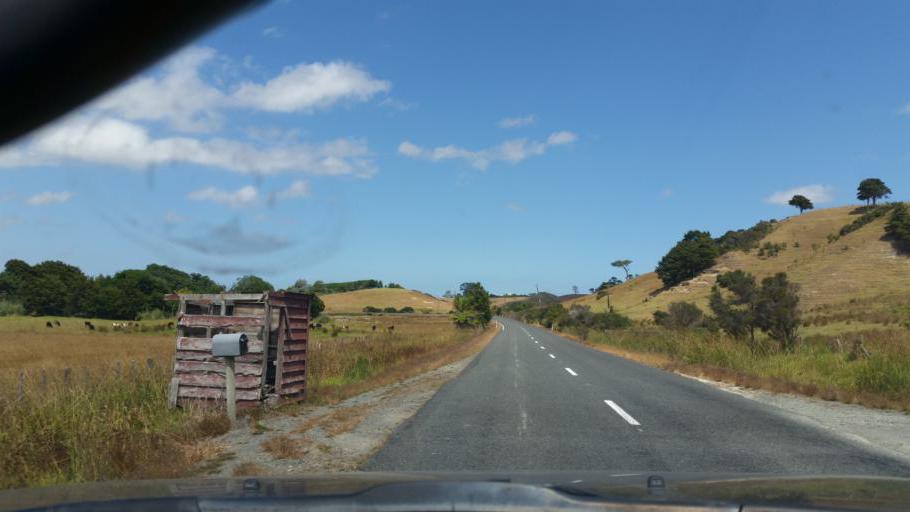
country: NZ
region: Northland
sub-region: Kaipara District
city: Dargaville
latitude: -35.8956
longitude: 173.8411
